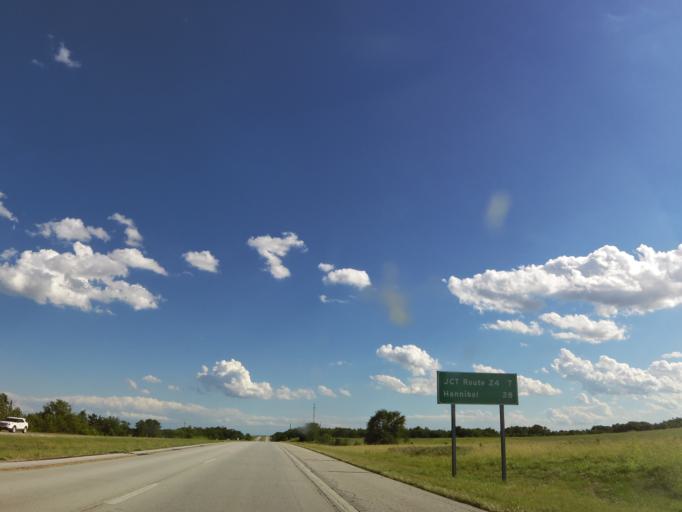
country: US
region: Missouri
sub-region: Lewis County
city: Canton
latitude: 40.0373
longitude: -91.5257
